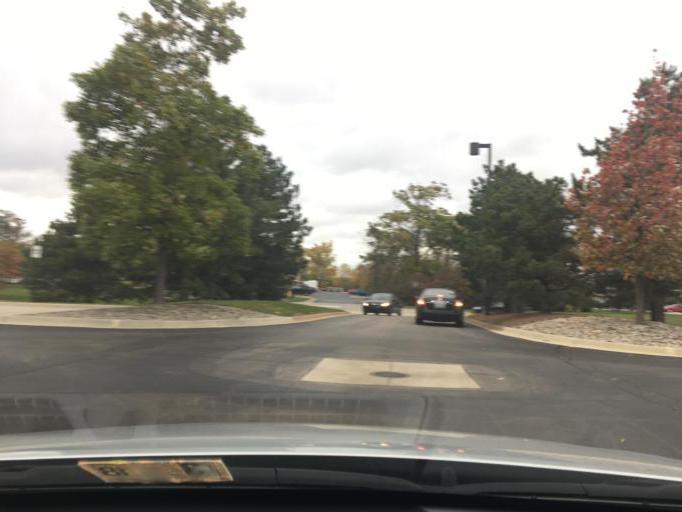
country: US
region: Michigan
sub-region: Wayne County
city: Melvindale
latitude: 42.2945
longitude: -83.2023
